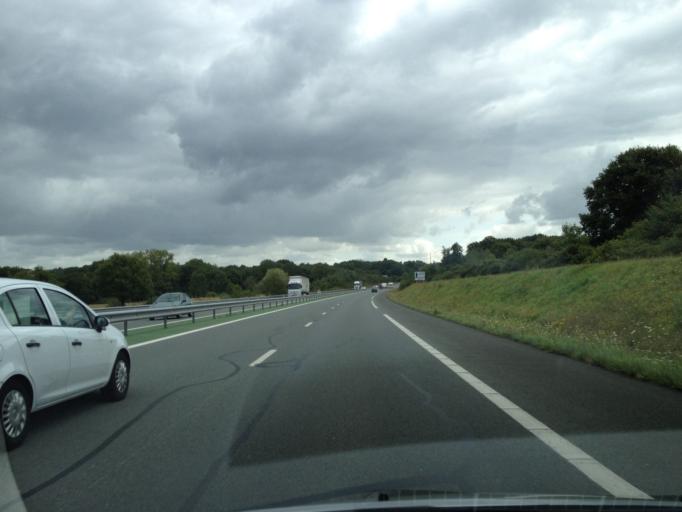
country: FR
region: Pays de la Loire
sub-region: Departement de la Vendee
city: La Verrie
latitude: 46.9341
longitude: -1.0056
